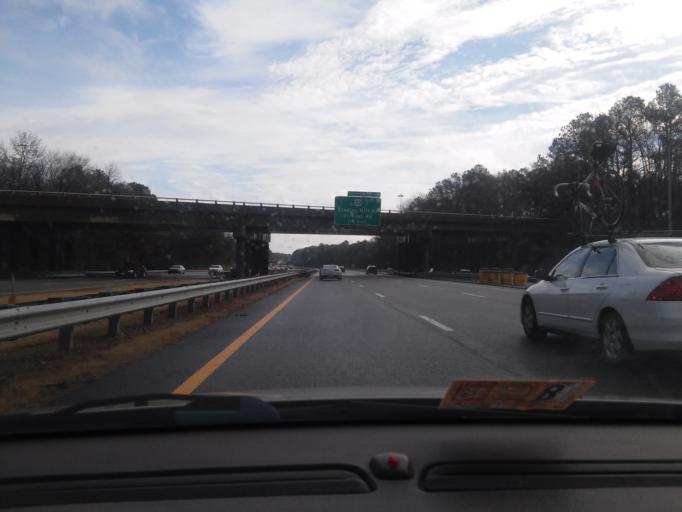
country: US
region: Virginia
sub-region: Henrico County
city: Dumbarton
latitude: 37.6057
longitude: -77.5171
